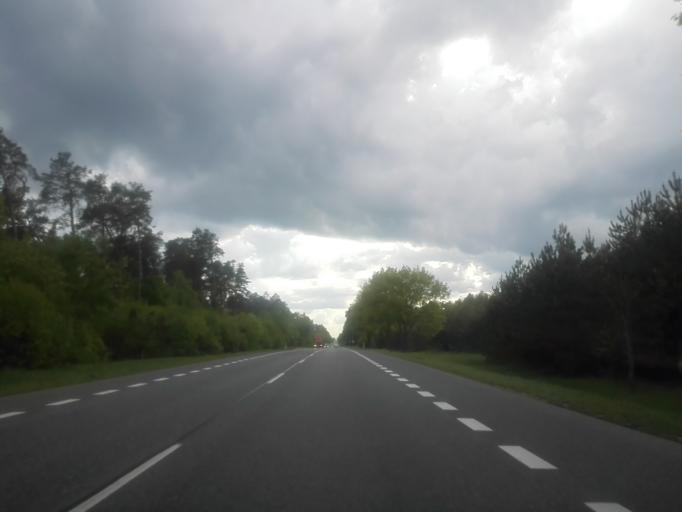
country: PL
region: Masovian Voivodeship
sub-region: Powiat ostrowski
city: Ostrow Mazowiecka
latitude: 52.8422
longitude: 21.9660
